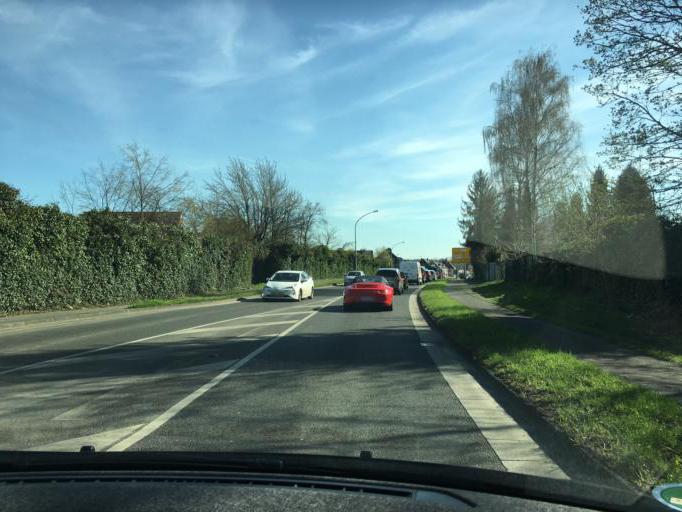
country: DE
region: North Rhine-Westphalia
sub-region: Regierungsbezirk Dusseldorf
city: Monchengladbach
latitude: 51.2060
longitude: 6.4746
